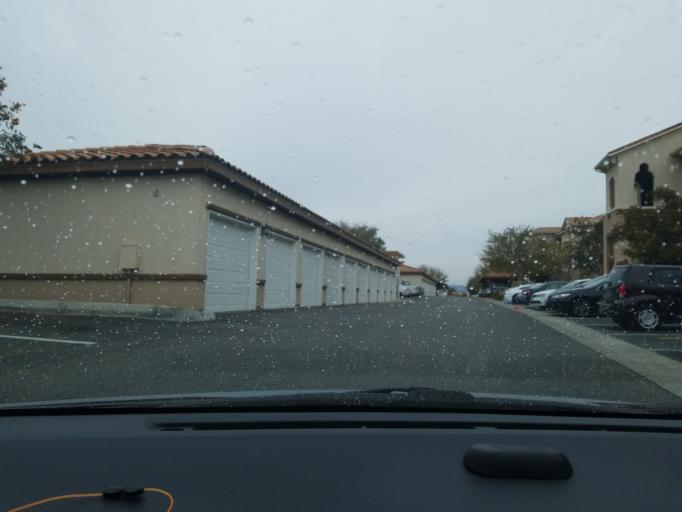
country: US
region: California
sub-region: Riverside County
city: Temecula
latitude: 33.4868
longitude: -117.1485
